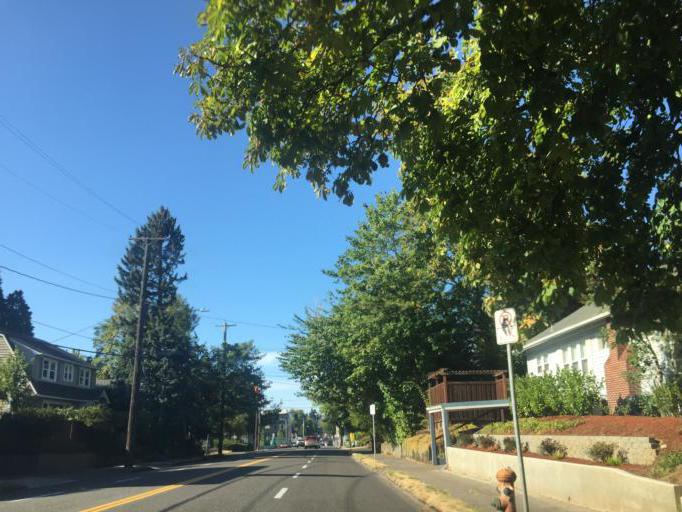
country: US
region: Oregon
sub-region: Multnomah County
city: Portland
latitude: 45.5323
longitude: -122.6306
